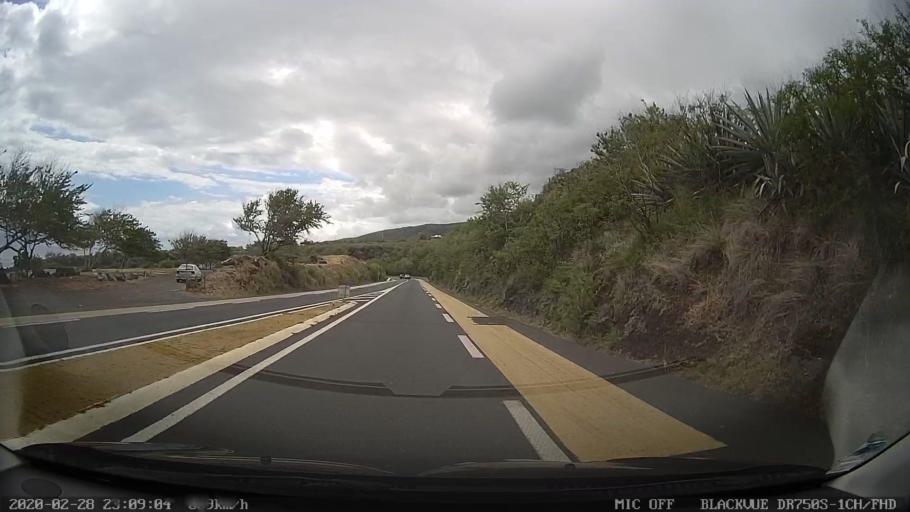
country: RE
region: Reunion
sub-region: Reunion
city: Trois-Bassins
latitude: -21.1287
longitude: 55.2695
